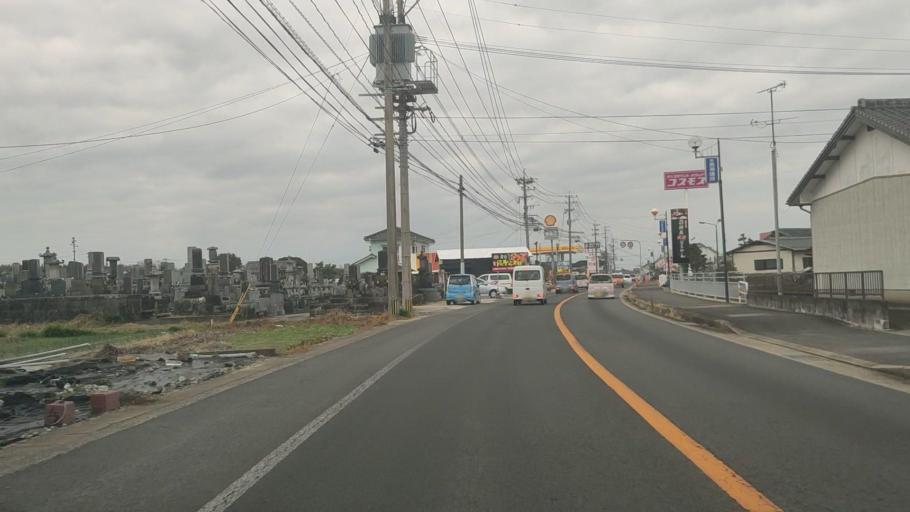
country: JP
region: Nagasaki
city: Shimabara
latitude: 32.8598
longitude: 130.3273
